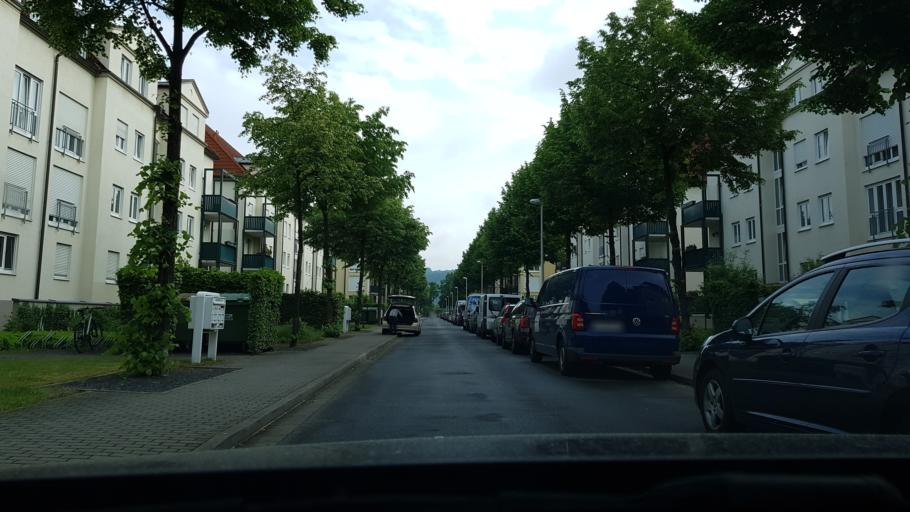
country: DE
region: Saxony
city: Heidenau
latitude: 51.0185
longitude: 13.8342
